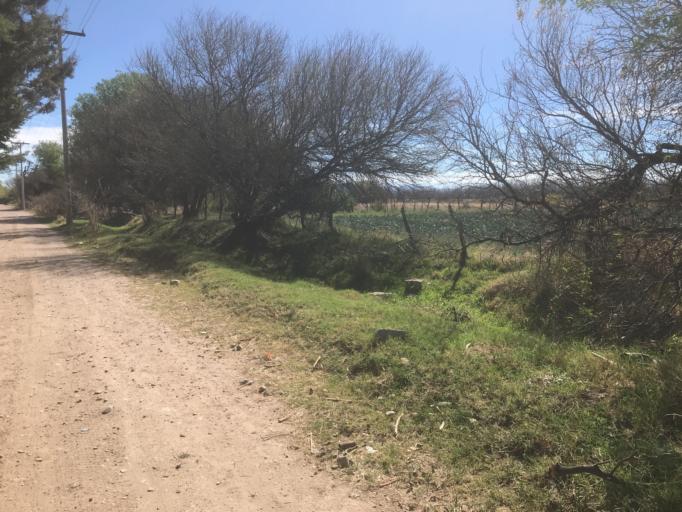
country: MX
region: Durango
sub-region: Durango
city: Sebastian Lerdo de Tejada
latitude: 23.9750
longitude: -104.6222
